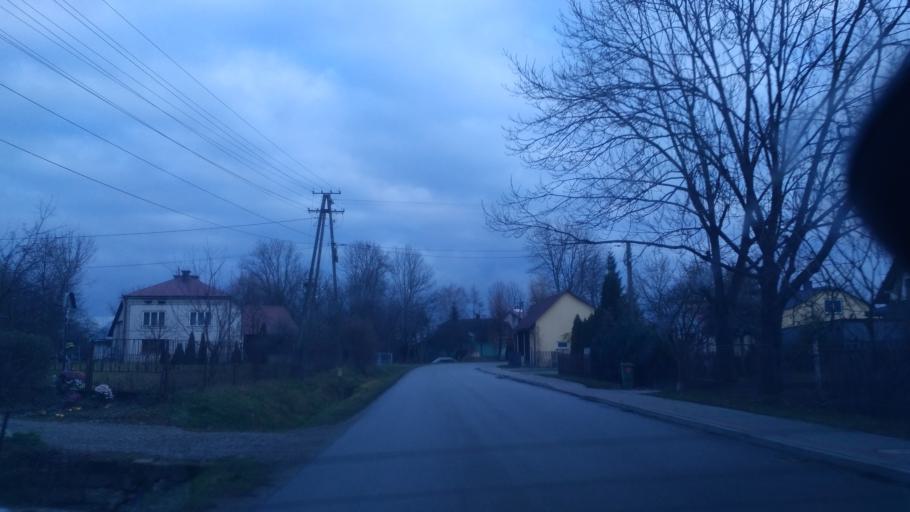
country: PL
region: Subcarpathian Voivodeship
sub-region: Powiat lancucki
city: Czarna
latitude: 50.1017
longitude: 22.1515
